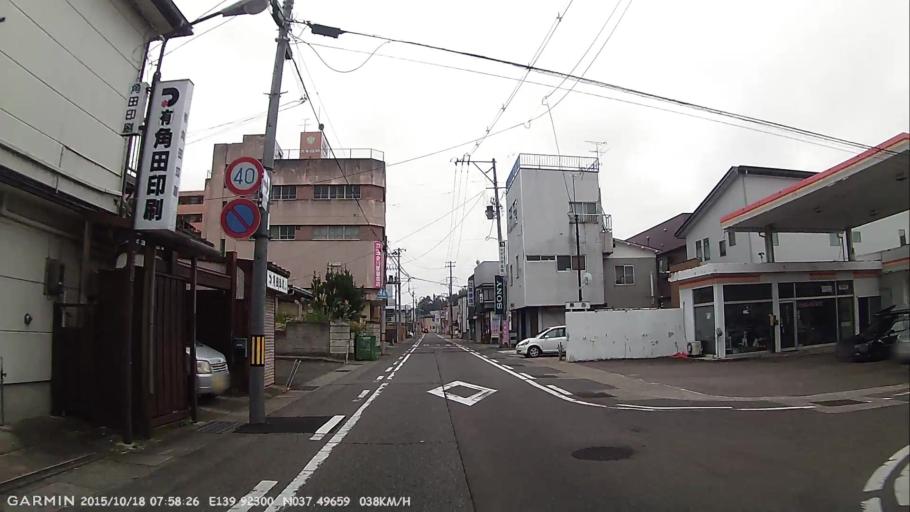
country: JP
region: Fukushima
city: Kitakata
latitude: 37.4965
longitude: 139.9230
